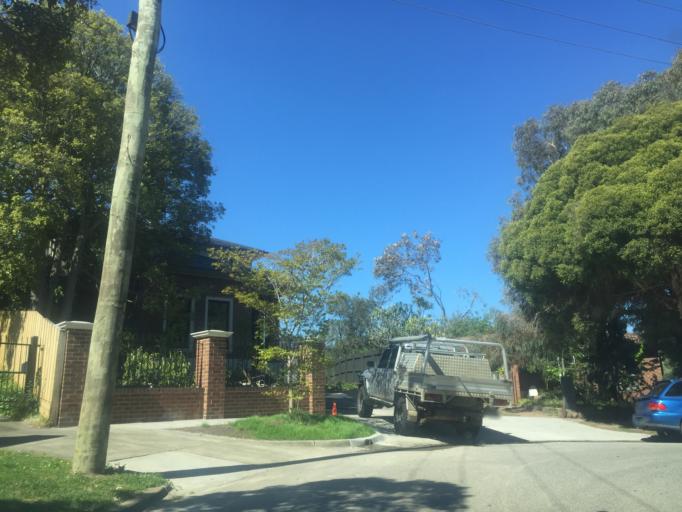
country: AU
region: Victoria
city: Mont Albert
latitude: -37.8125
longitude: 145.0958
